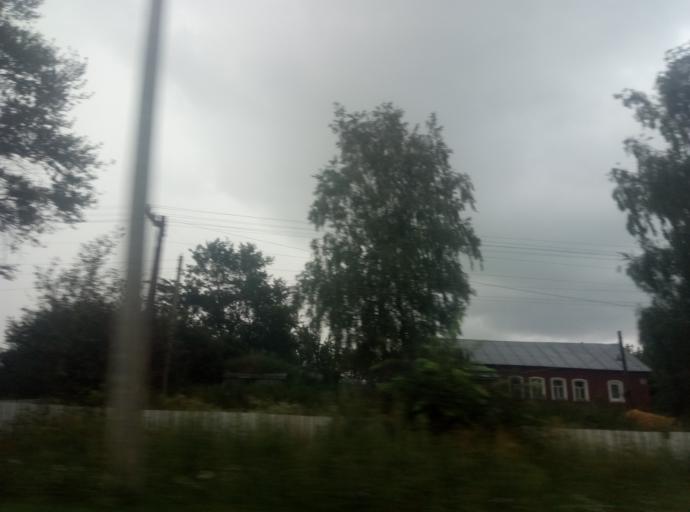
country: RU
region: Tula
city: Kireyevsk
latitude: 53.9932
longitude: 37.9271
